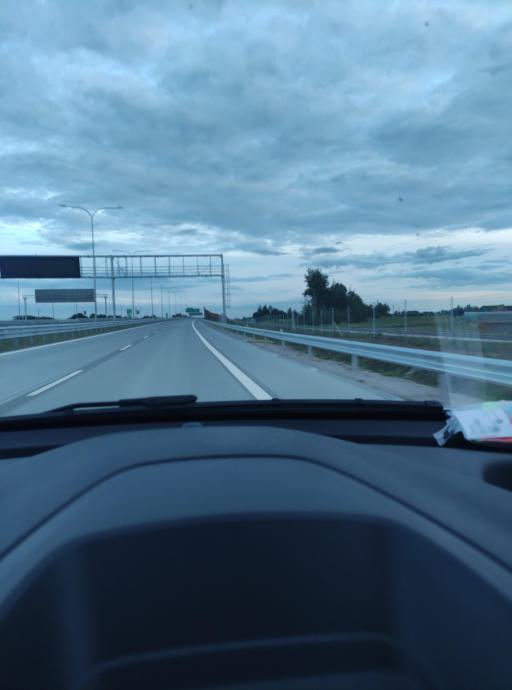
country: PL
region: Masovian Voivodeship
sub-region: Powiat piaseczynski
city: Mysiadlo
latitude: 52.1332
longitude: 20.9893
